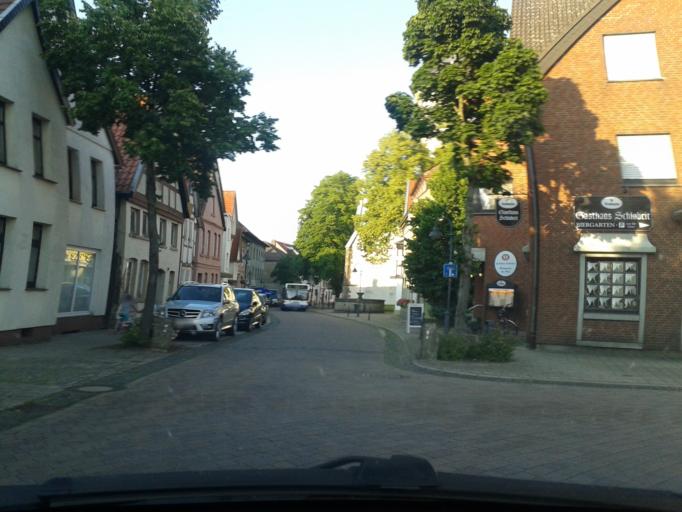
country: DE
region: North Rhine-Westphalia
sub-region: Regierungsbezirk Detmold
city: Horn
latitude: 51.8717
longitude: 8.9412
